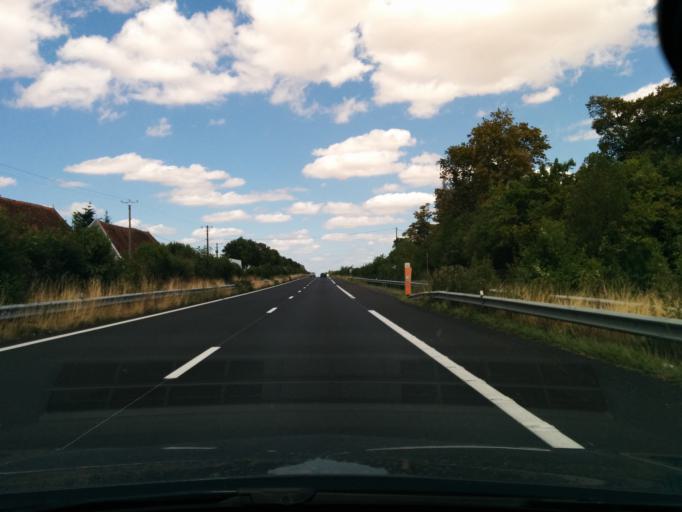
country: FR
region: Centre
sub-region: Departement de l'Indre
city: Montierchaume
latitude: 46.9556
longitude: 1.7575
